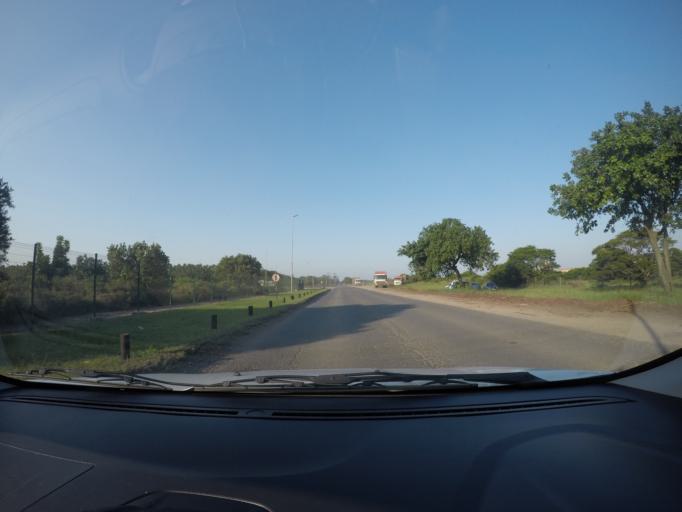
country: ZA
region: KwaZulu-Natal
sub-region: uThungulu District Municipality
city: Richards Bay
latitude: -28.7633
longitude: 32.0006
